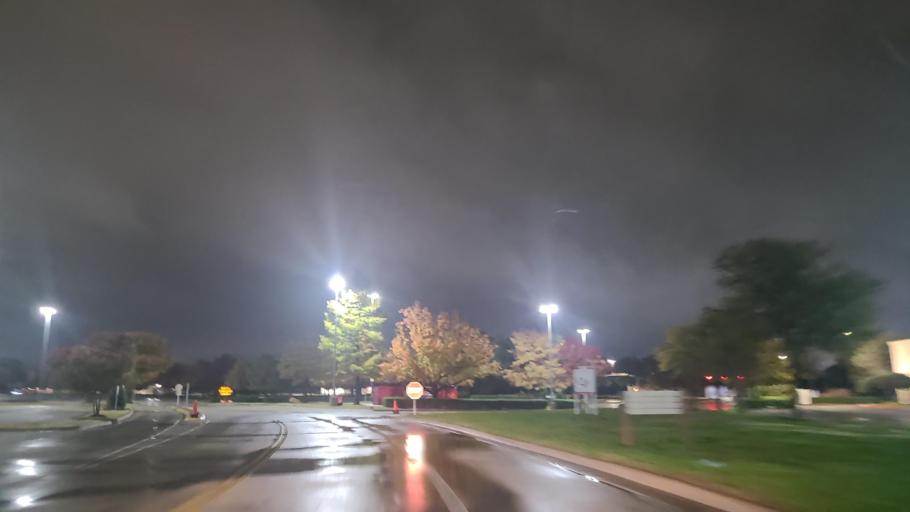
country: US
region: Texas
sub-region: Tarrant County
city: Dalworthington Gardens
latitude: 32.6807
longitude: -97.1266
